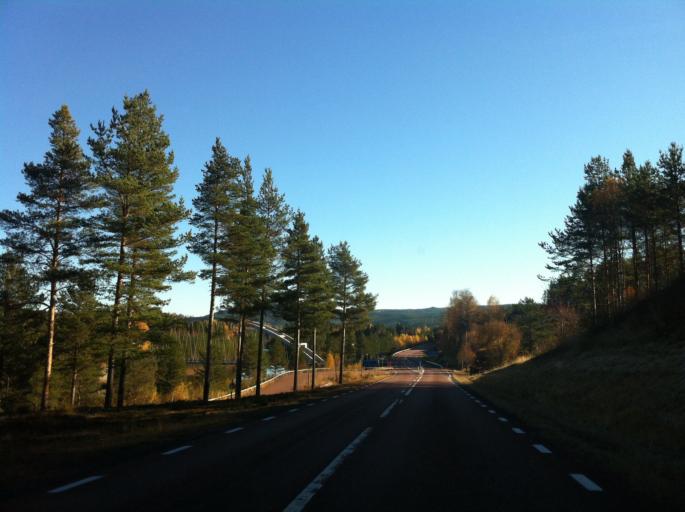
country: SE
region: Dalarna
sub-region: Alvdalens Kommun
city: AElvdalen
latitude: 61.2900
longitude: 13.7426
